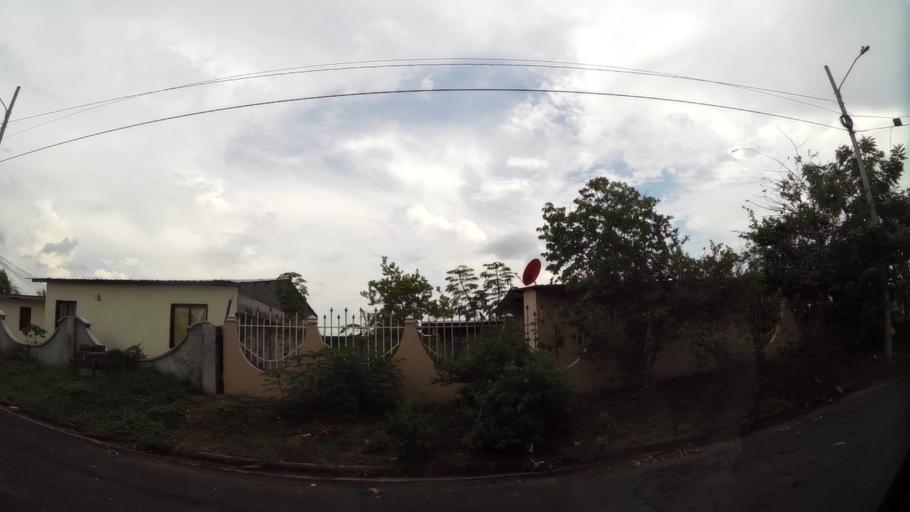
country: PA
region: Panama
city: Cabra Numero Uno
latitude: 9.0936
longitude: -79.3468
